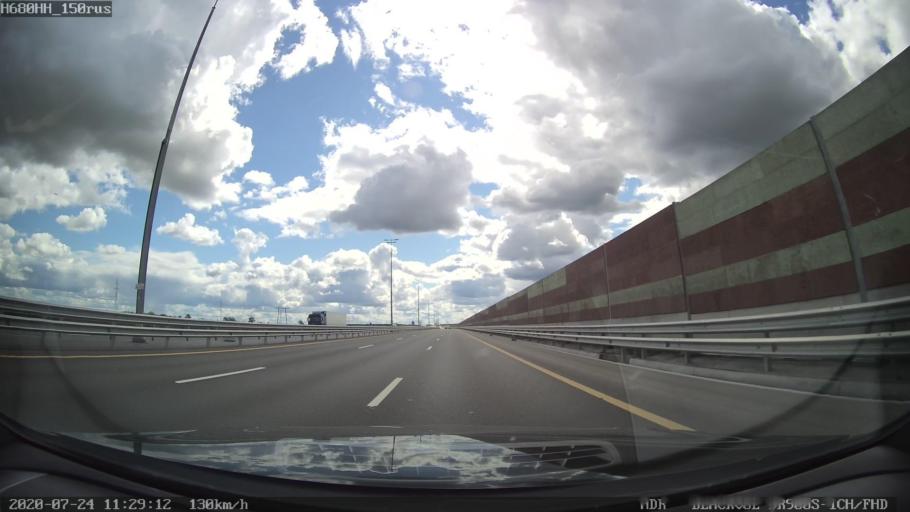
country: RU
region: Leningrad
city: Fedorovskoye
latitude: 59.6893
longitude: 30.5765
